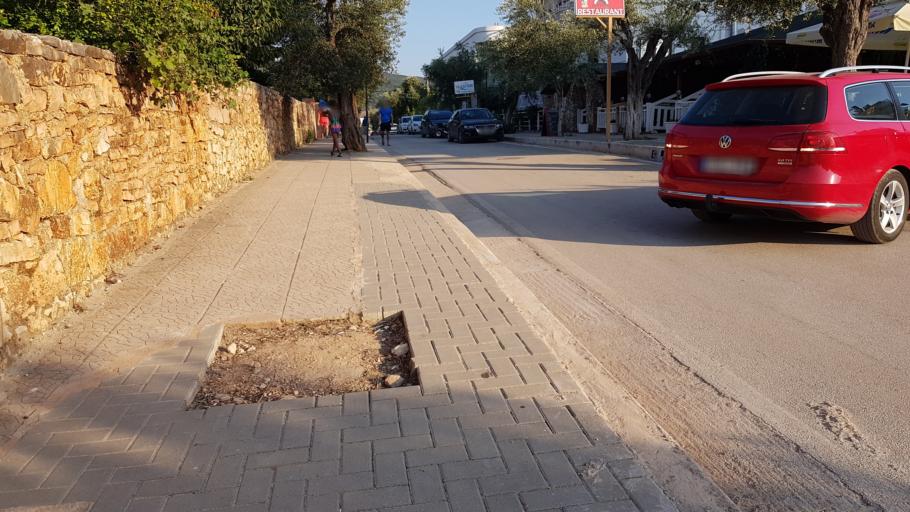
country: AL
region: Vlore
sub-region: Rrethi i Sarandes
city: Xarre
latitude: 39.7719
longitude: 20.0026
